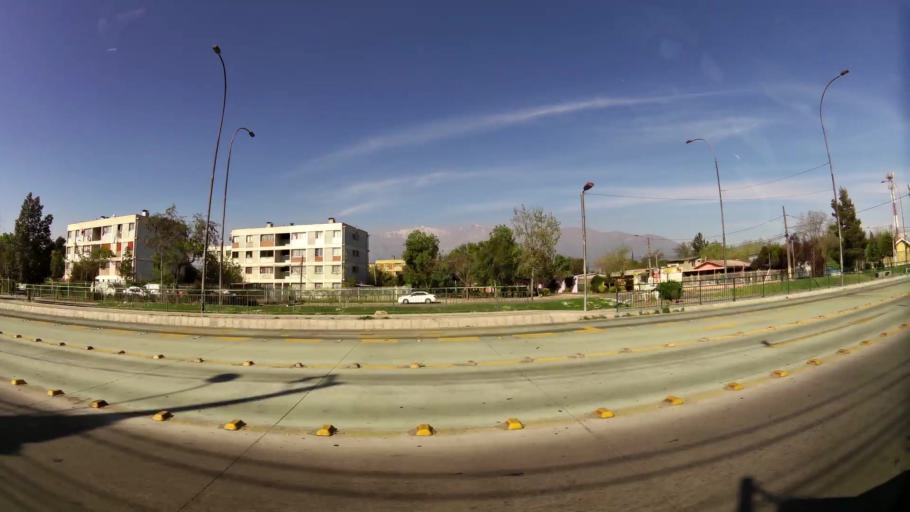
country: CL
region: Santiago Metropolitan
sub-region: Provincia de Santiago
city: Santiago
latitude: -33.5087
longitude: -70.6260
